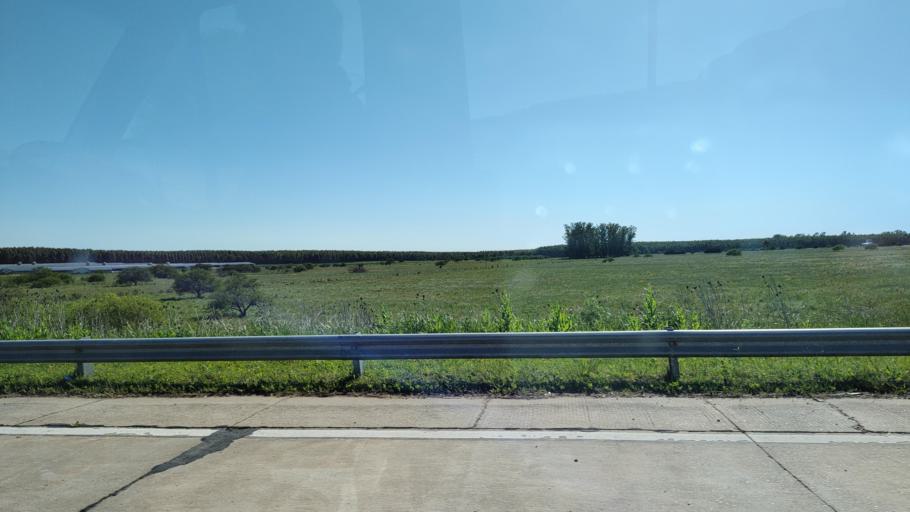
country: AR
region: Entre Rios
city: Villa Elisa
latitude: -32.0366
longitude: -58.2746
